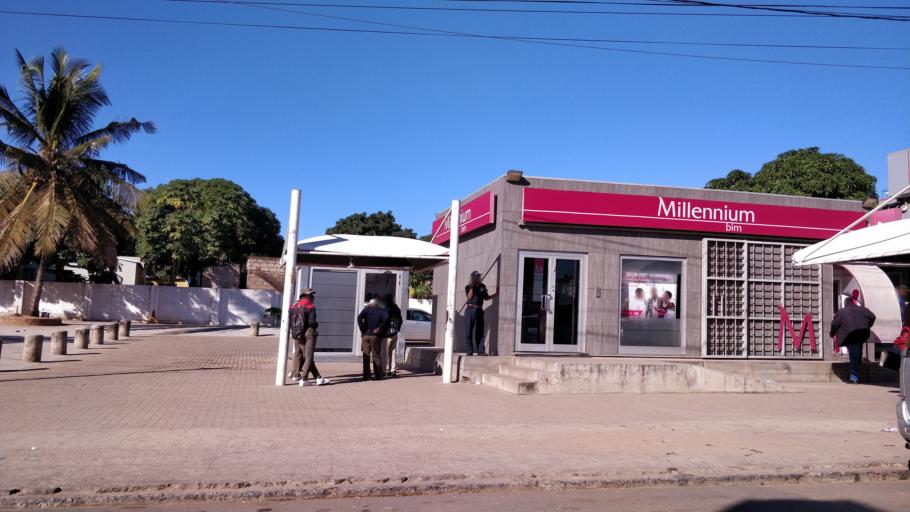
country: MZ
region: Maputo City
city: Maputo
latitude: -25.9271
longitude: 32.6042
